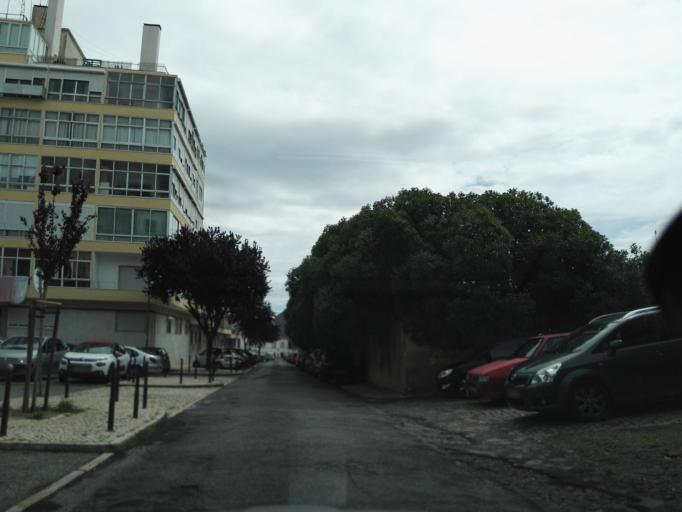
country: PT
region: Setubal
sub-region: Almada
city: Pragal
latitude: 38.7026
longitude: -9.1916
